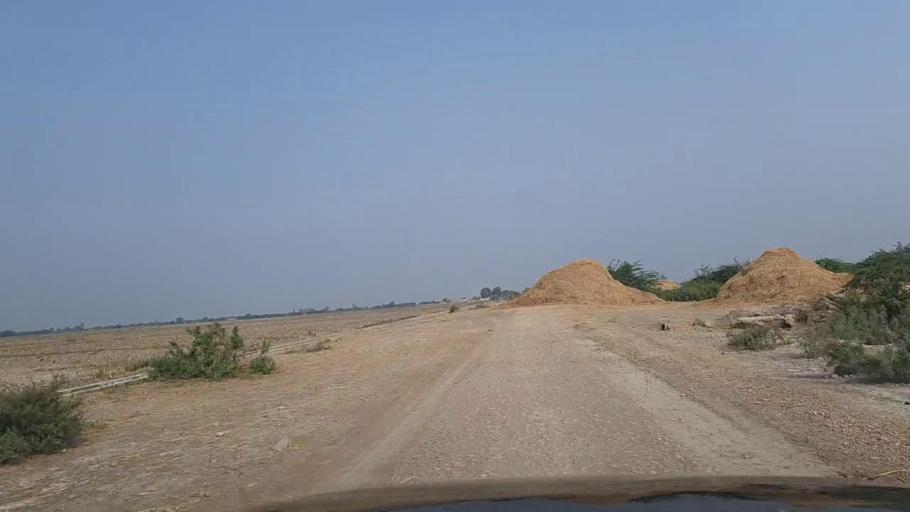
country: PK
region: Sindh
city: Thatta
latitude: 24.7609
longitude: 67.8715
